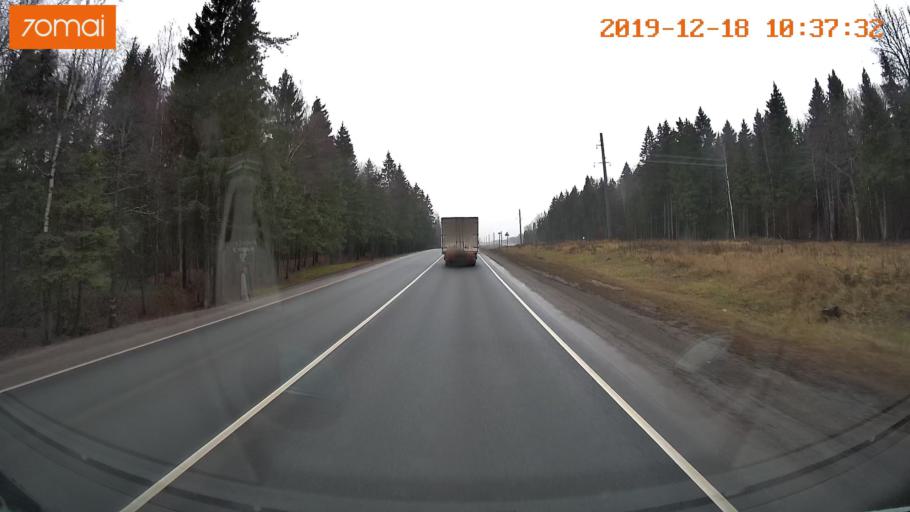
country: RU
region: Moskovskaya
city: Troitsk
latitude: 55.4288
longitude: 37.1693
